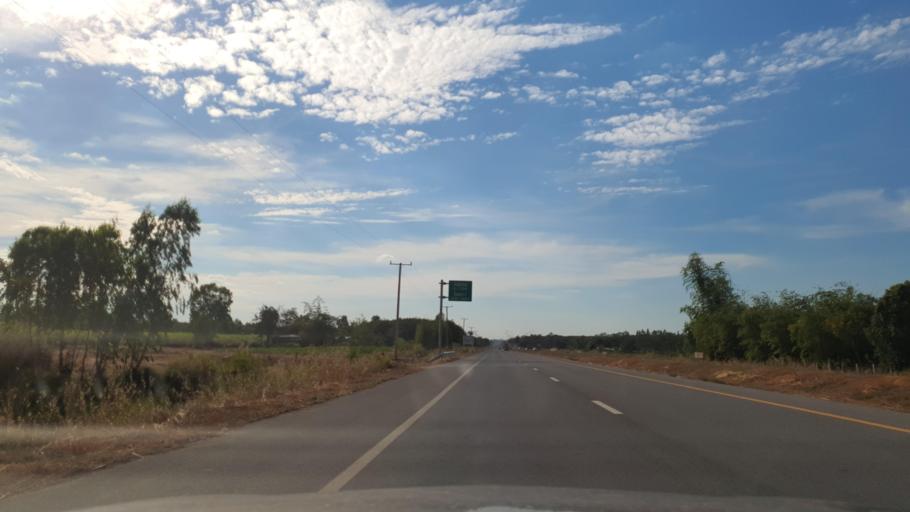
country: TH
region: Roi Et
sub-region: Amphoe Pho Chai
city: Pho Chai
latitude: 16.4143
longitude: 103.7964
